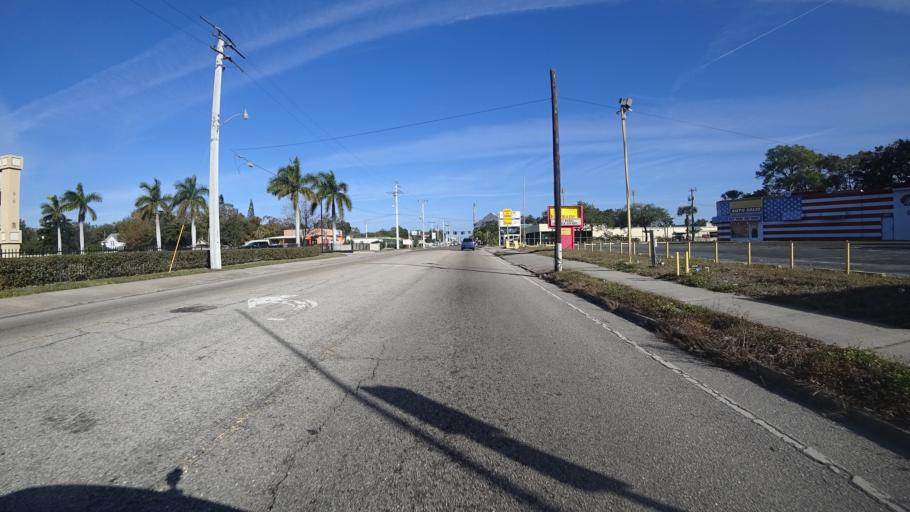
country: US
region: Florida
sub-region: Manatee County
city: Bradenton
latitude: 27.4829
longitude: -82.5711
